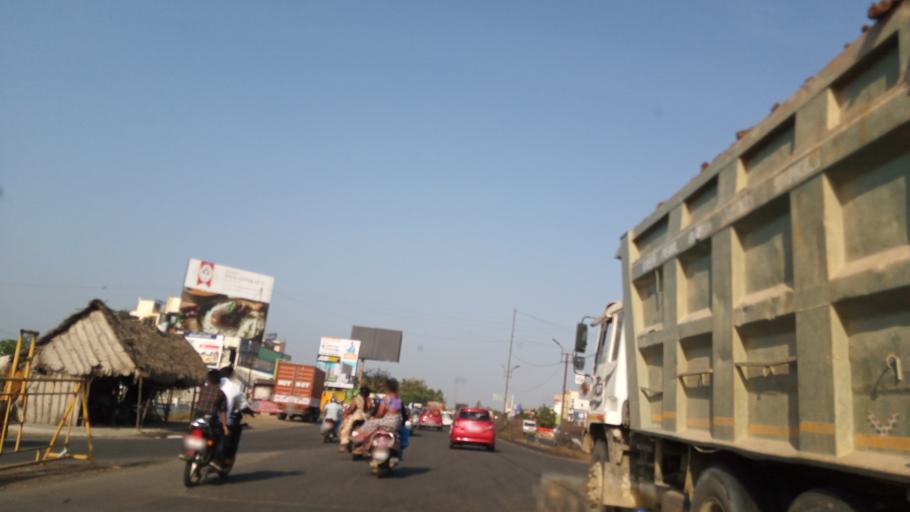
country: IN
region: Tamil Nadu
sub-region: Kancheepuram
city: Poonamalle
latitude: 13.0456
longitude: 80.0701
